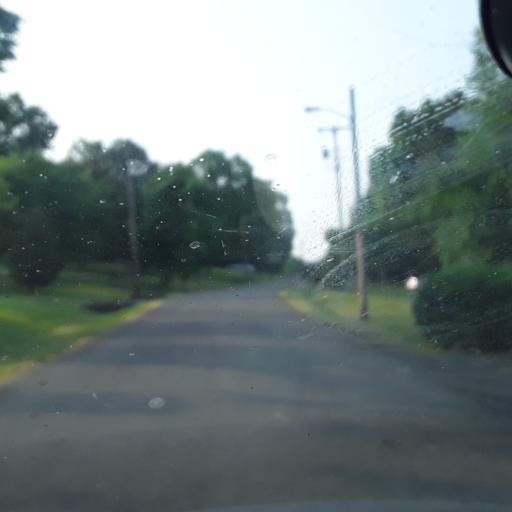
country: US
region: Tennessee
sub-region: Williamson County
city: Brentwood Estates
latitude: 36.0546
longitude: -86.7237
